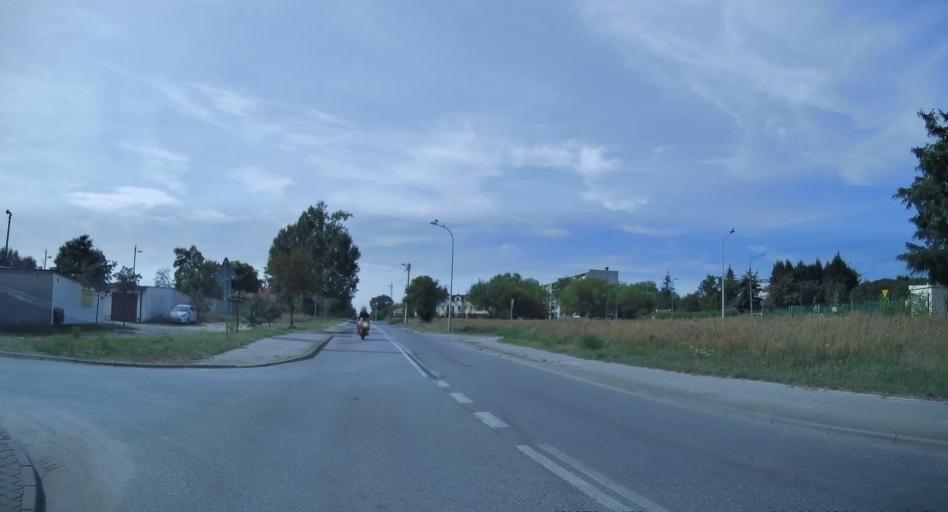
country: PL
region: Lodz Voivodeship
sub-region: Powiat tomaszowski
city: Tomaszow Mazowiecki
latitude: 51.5400
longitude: 20.0002
